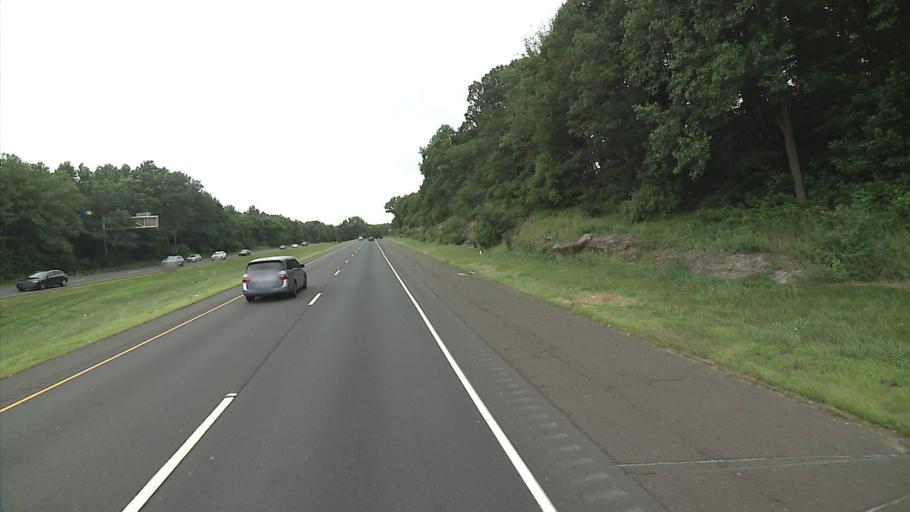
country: US
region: Connecticut
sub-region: Fairfield County
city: Shelton
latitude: 41.2684
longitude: -73.1240
